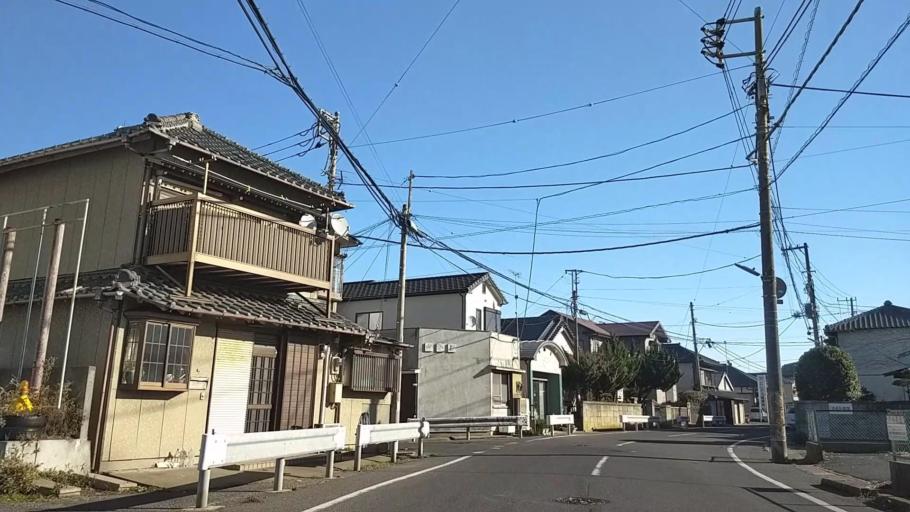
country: JP
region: Chiba
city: Hasaki
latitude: 35.7372
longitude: 140.8497
